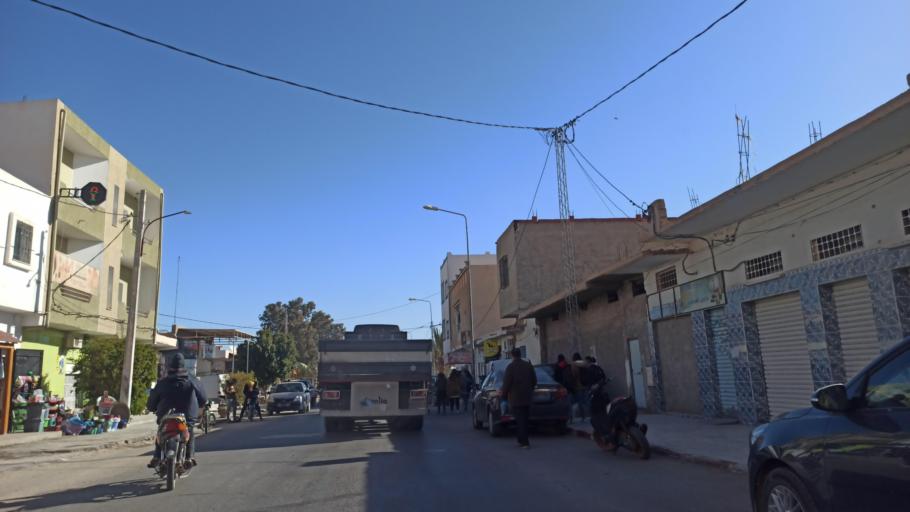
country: TN
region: Gafsa
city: Al Metlaoui
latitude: 34.3149
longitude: 8.4079
